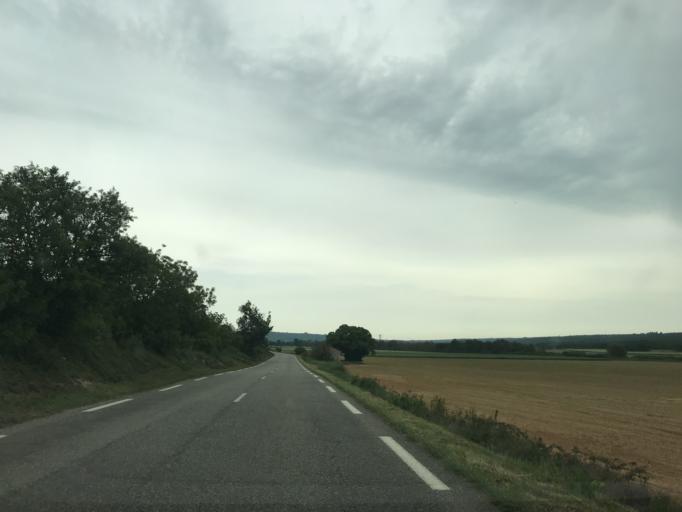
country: FR
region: Provence-Alpes-Cote d'Azur
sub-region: Departement du Var
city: Ginasservis
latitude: 43.6425
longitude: 5.8083
